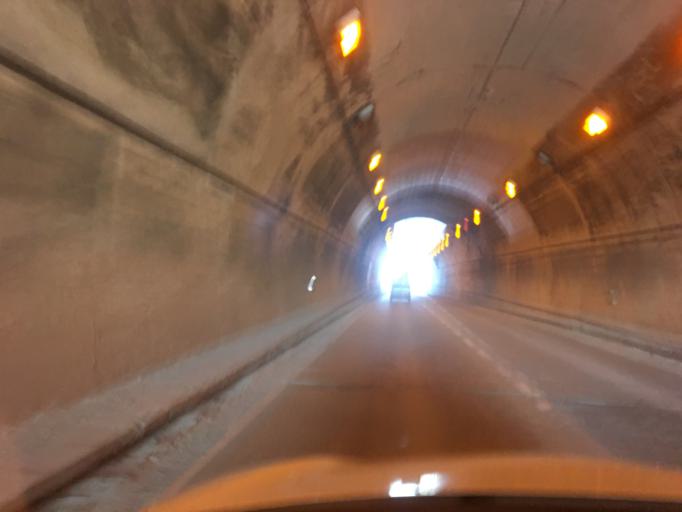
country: JP
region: Fukushima
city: Iwaki
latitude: 36.9978
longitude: 140.9667
